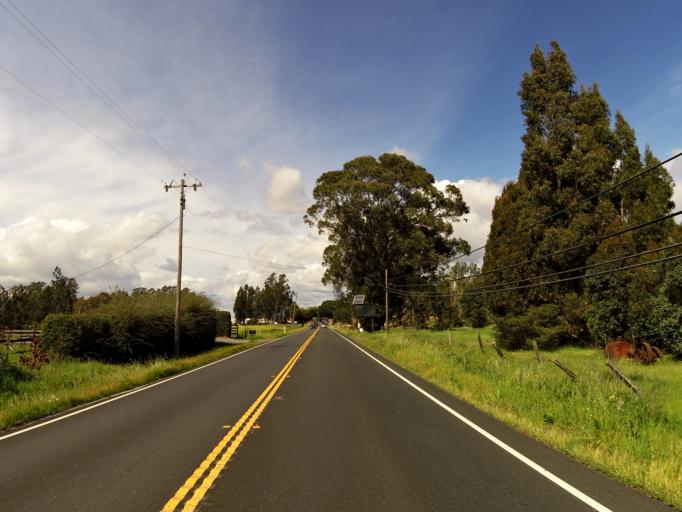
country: US
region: California
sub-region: Sonoma County
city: Temelec
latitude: 38.2317
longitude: -122.4598
